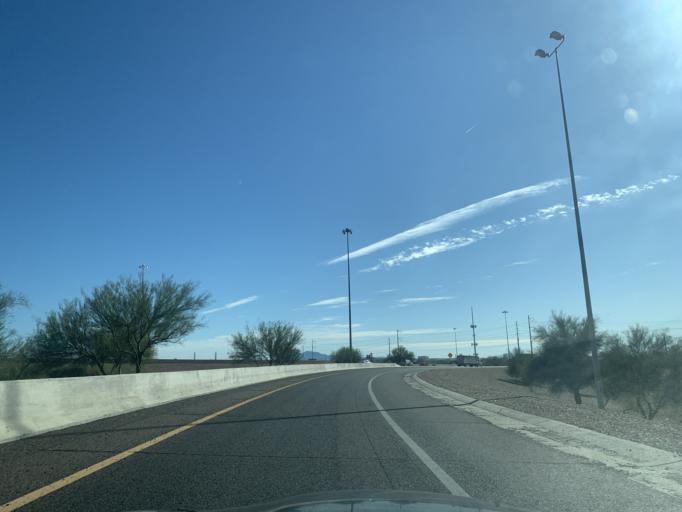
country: US
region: Arizona
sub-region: Maricopa County
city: Guadalupe
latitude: 33.2950
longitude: -111.9749
